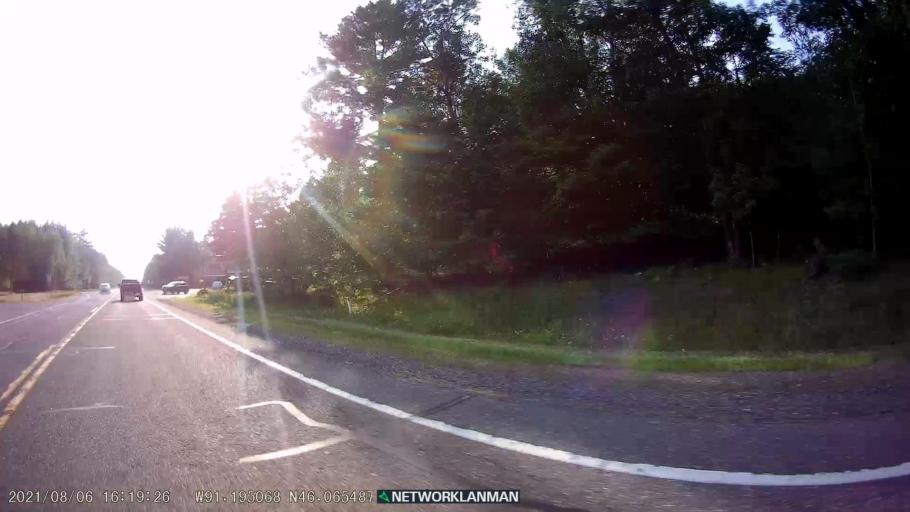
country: US
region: Wisconsin
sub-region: Sawyer County
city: Little Round Lake
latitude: 46.0655
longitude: -91.1953
